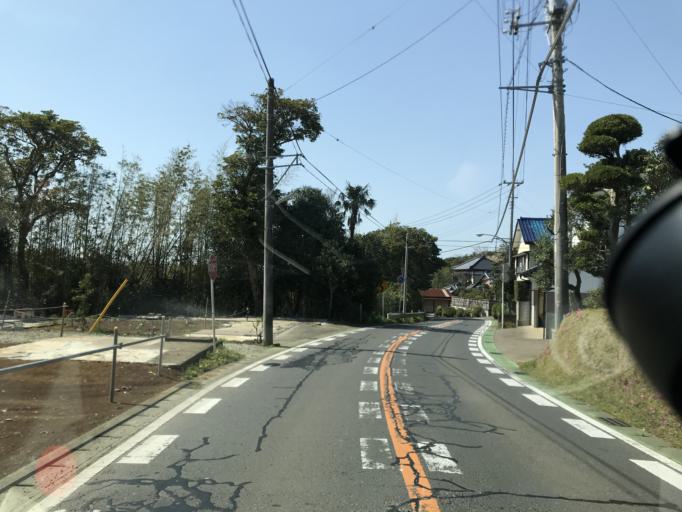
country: JP
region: Chiba
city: Asahi
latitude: 35.7930
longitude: 140.6743
